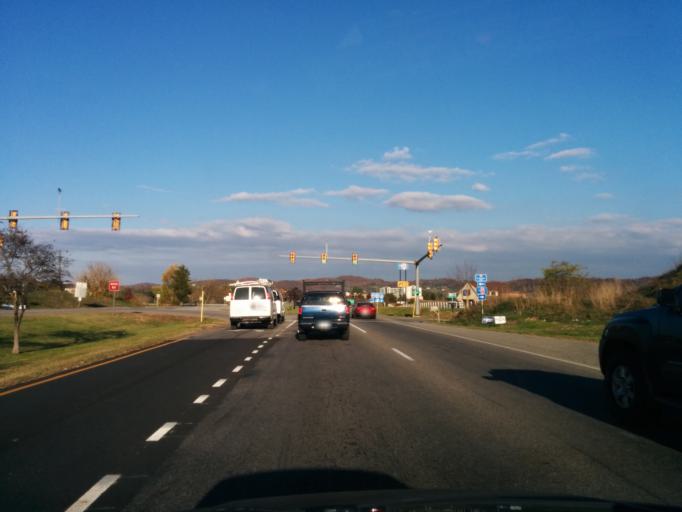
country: US
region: Virginia
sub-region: Rockbridge County
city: East Lexington
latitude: 37.7991
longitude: -79.4188
